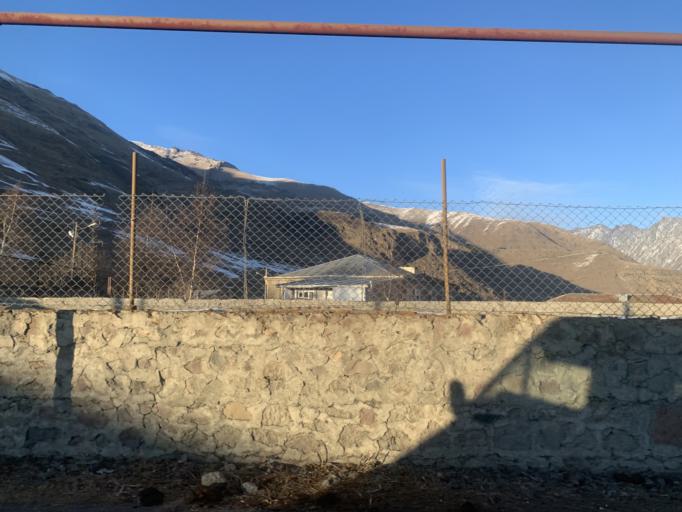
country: GE
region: Mtskheta-Mtianeti
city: Step'antsminda
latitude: 42.6141
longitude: 44.5916
